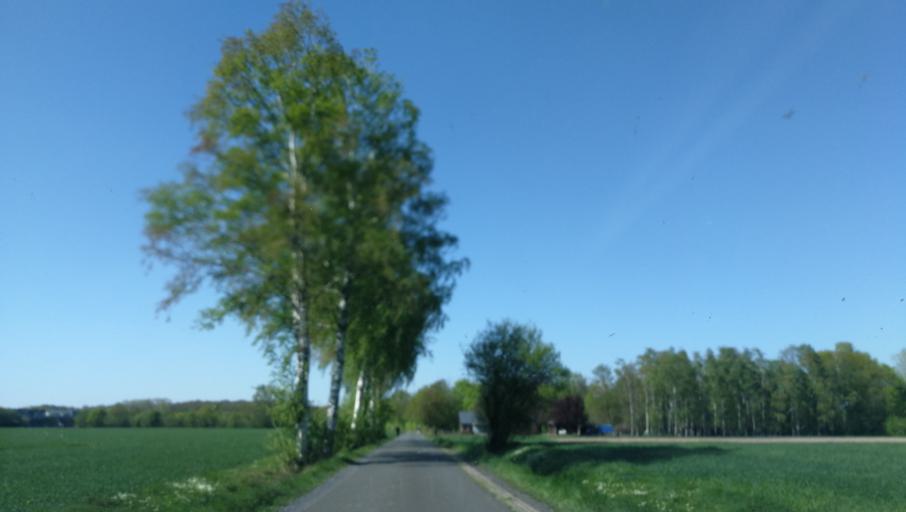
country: DE
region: North Rhine-Westphalia
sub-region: Regierungsbezirk Munster
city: Muenster
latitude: 51.9319
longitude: 7.5589
